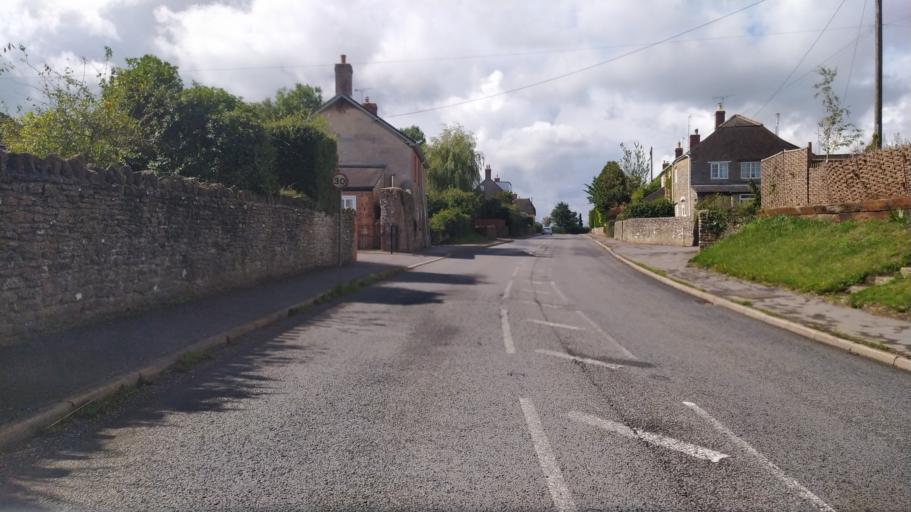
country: GB
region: England
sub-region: Somerset
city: Milborne Port
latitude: 50.9167
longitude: -2.4344
